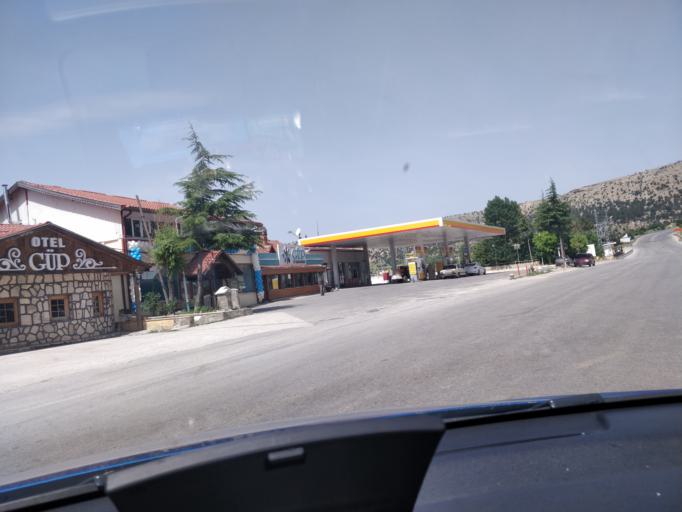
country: TR
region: Karaman
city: Bucakkisla
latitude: 36.8847
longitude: 33.2794
